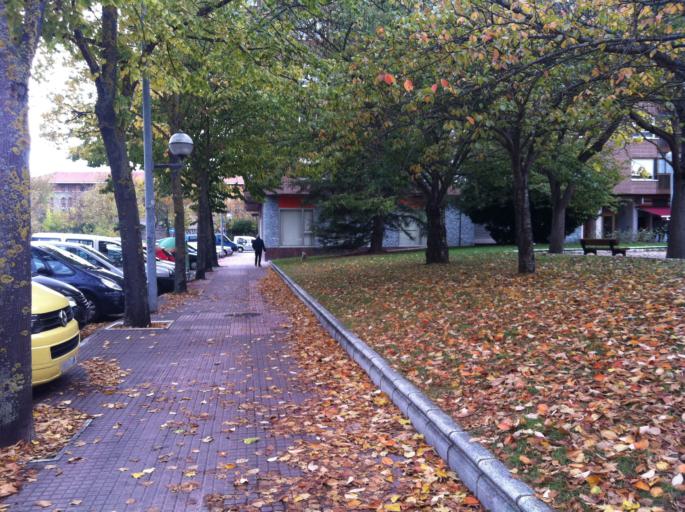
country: ES
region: Basque Country
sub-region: Provincia de Alava
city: Gasteiz / Vitoria
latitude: 42.8502
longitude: -2.6876
